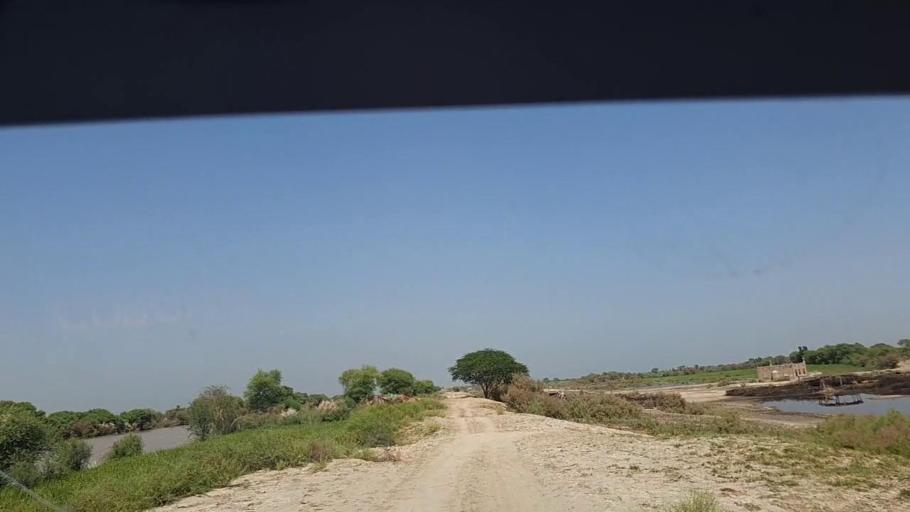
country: PK
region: Sindh
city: Kandhkot
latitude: 28.1802
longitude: 69.1528
